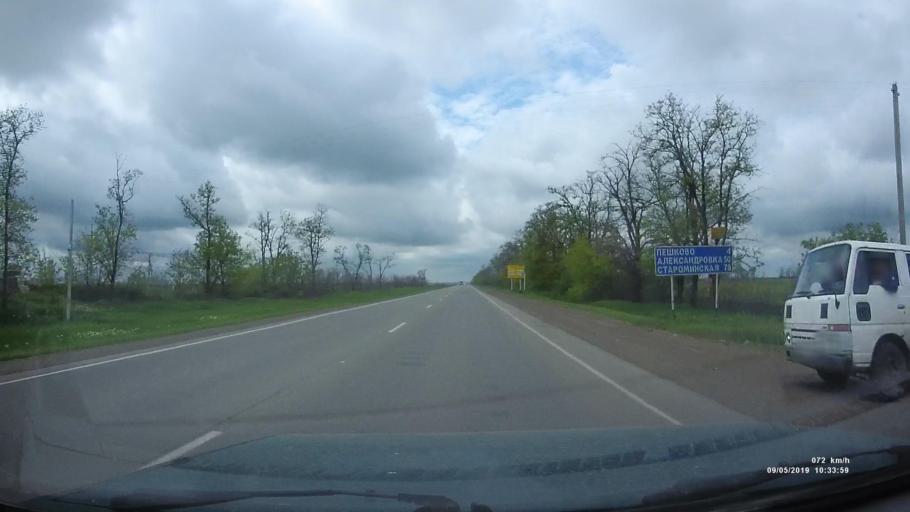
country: RU
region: Rostov
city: Azov
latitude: 47.0589
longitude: 39.4227
